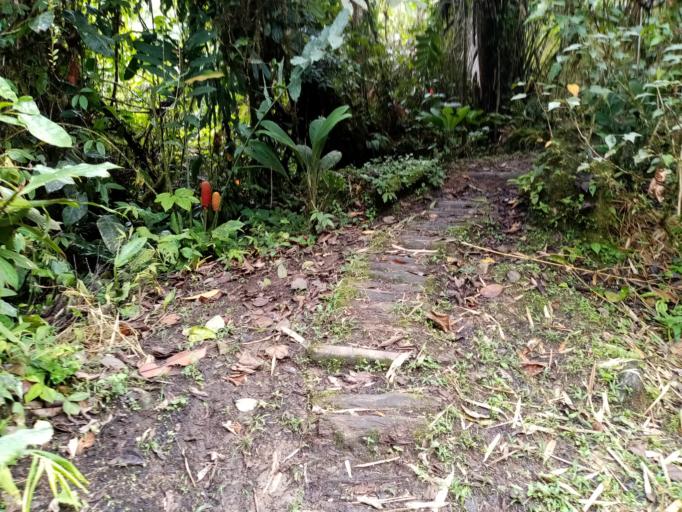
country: EC
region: Napo
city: Tena
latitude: -0.9712
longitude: -77.7998
